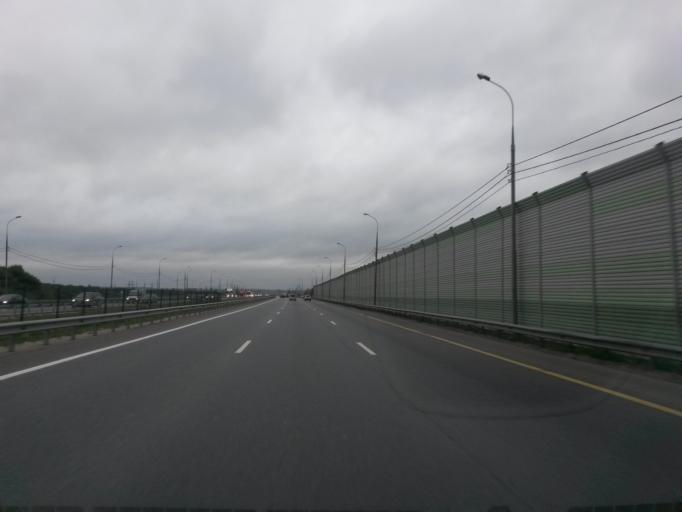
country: RU
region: Moskovskaya
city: Yam
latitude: 55.4777
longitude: 37.7476
